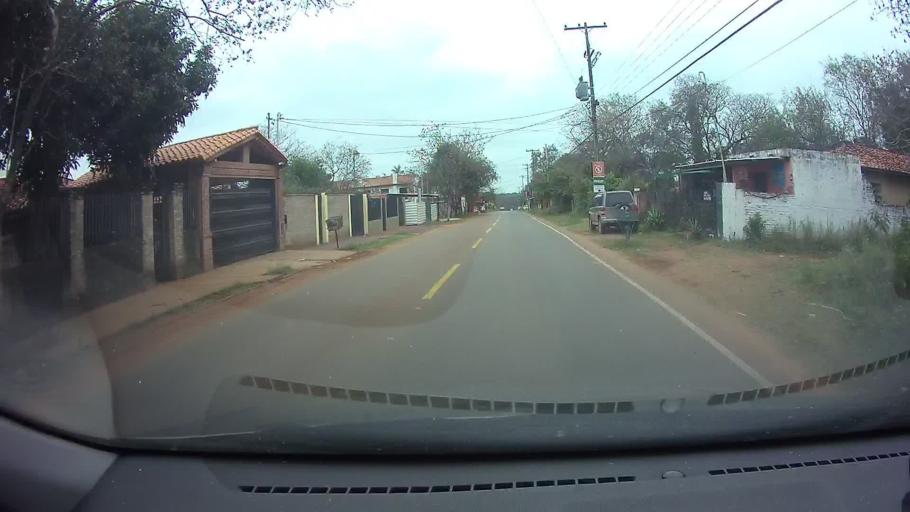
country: PY
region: Central
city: Limpio
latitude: -25.2477
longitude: -57.5003
